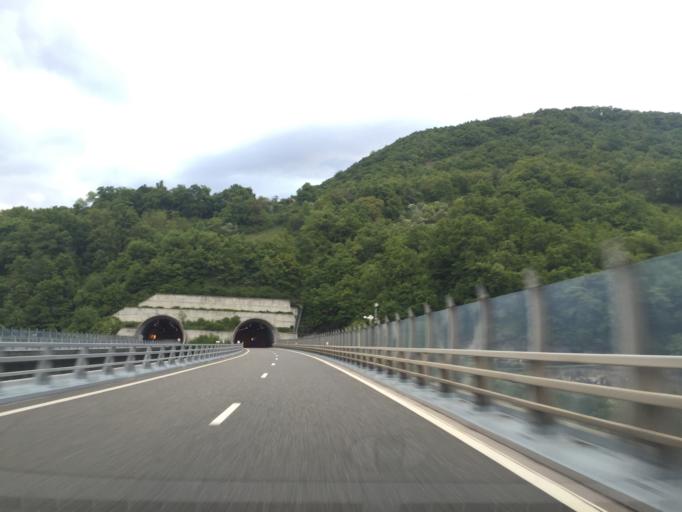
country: FR
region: Rhone-Alpes
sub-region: Departement de l'Isere
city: Vif
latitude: 45.0485
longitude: 5.6843
